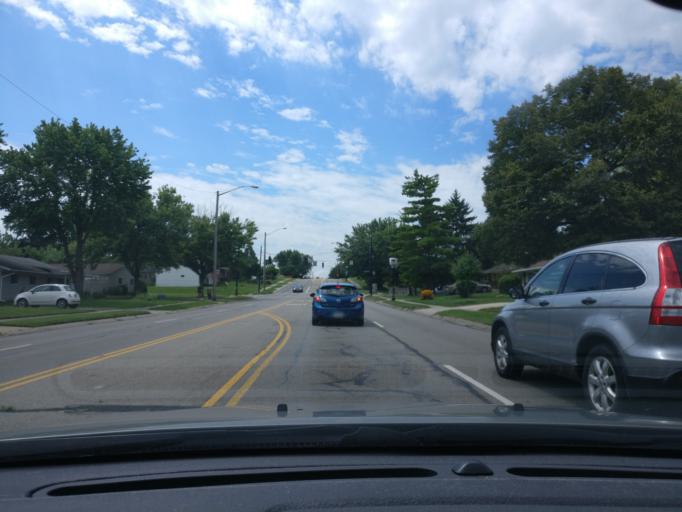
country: US
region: Ohio
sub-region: Montgomery County
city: West Carrollton City
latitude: 39.6594
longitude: -84.2420
